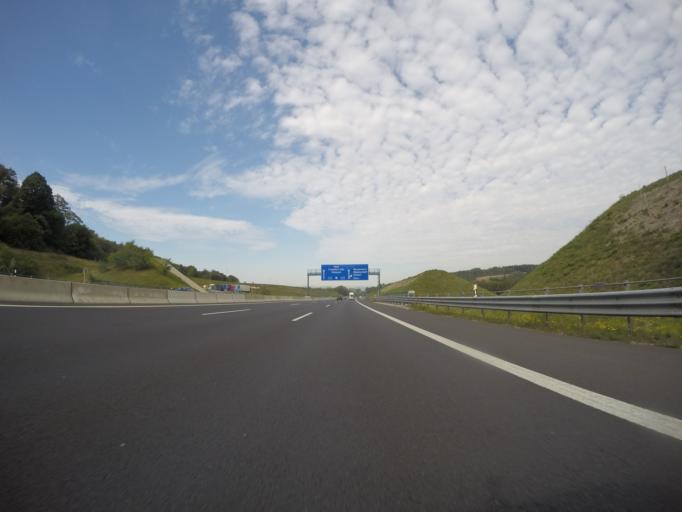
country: DE
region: Bavaria
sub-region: Regierungsbezirk Unterfranken
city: Waldaschaff
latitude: 49.9817
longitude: 9.2655
